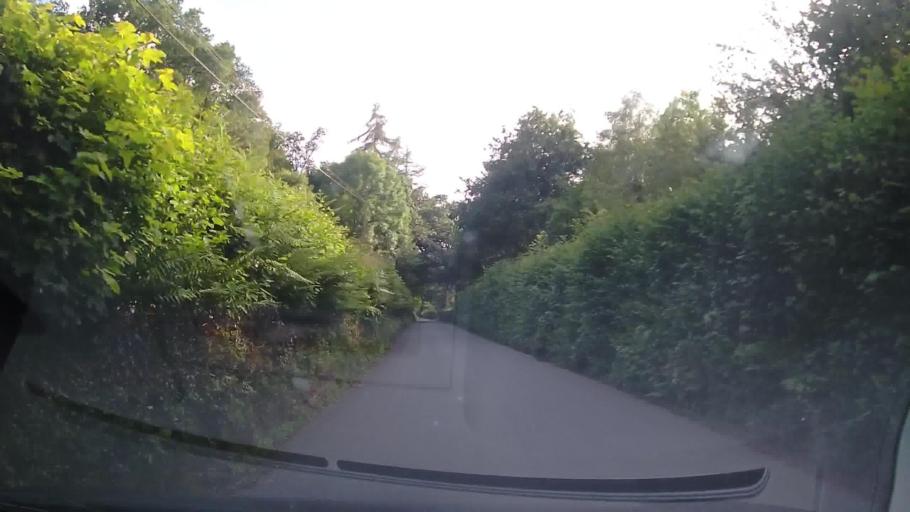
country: GB
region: Wales
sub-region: Gwynedd
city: Bala
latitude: 52.8942
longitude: -3.6039
